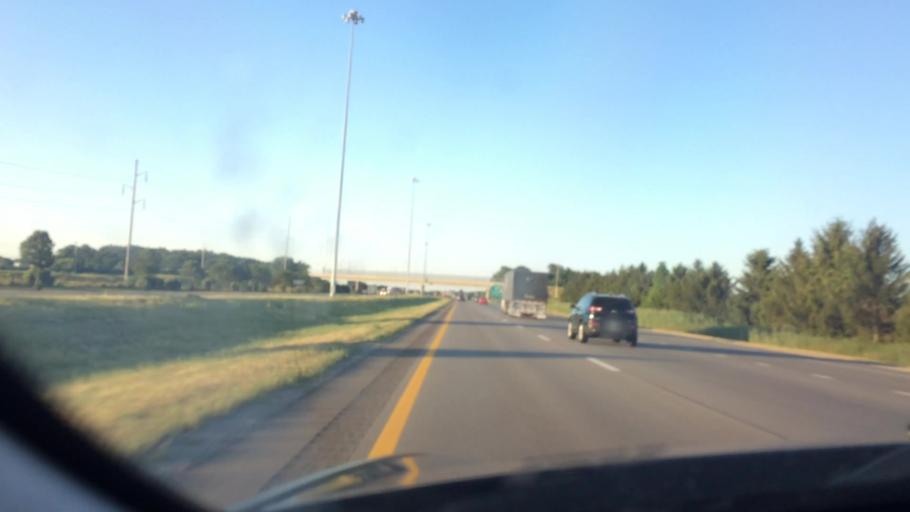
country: US
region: Ohio
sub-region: Lucas County
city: Maumee
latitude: 41.5746
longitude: -83.6914
